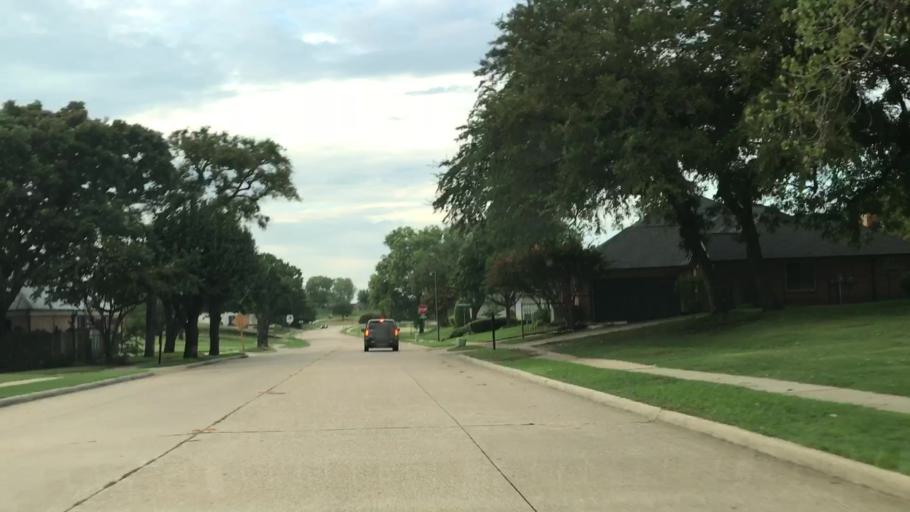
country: US
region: Texas
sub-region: Denton County
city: The Colony
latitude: 33.0371
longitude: -96.8466
